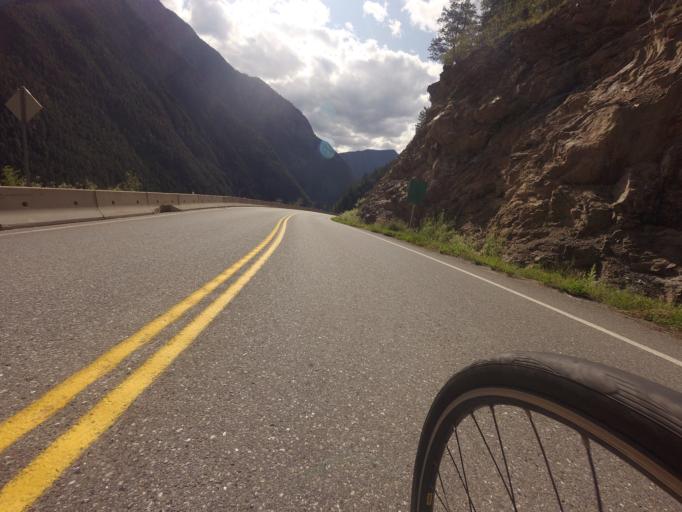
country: CA
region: British Columbia
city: Lillooet
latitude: 50.6423
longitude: -122.0289
